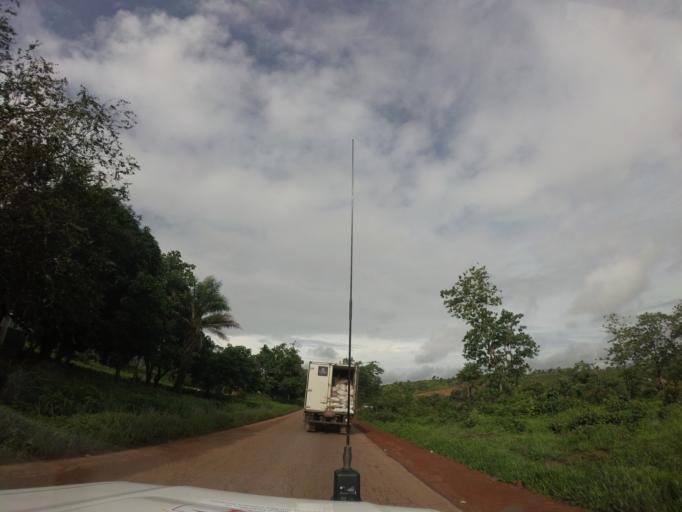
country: GN
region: Kindia
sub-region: Coyah
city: Coyah
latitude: 9.8112
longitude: -13.2721
